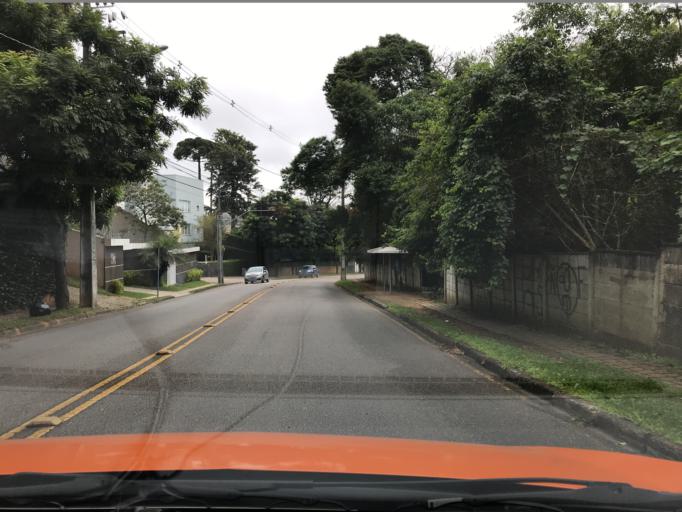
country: BR
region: Parana
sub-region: Curitiba
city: Curitiba
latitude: -25.4238
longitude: -49.3024
